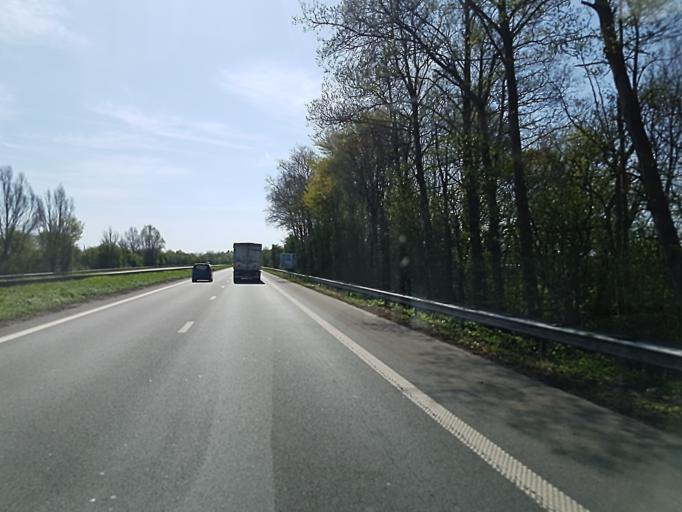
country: BE
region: Wallonia
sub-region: Province du Hainaut
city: Pecq
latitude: 50.6395
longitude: 3.3036
